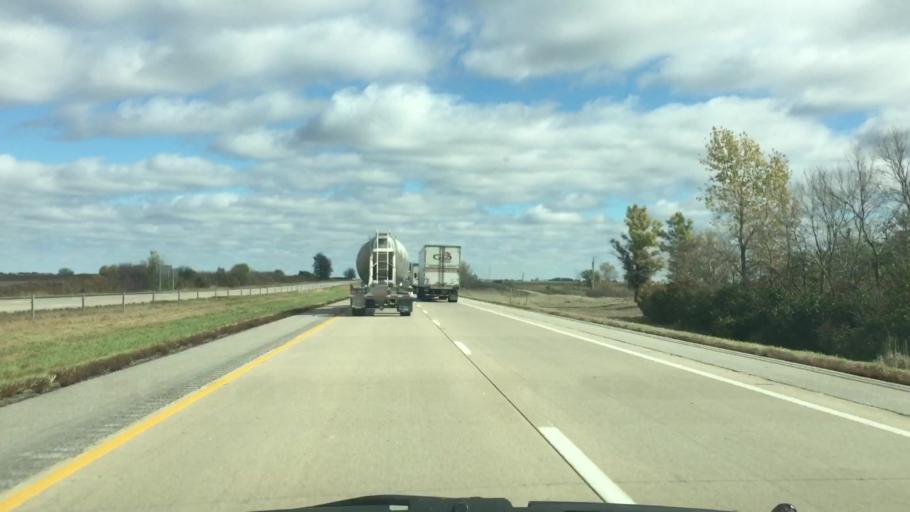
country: US
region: Iowa
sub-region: Poweshiek County
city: Brooklyn
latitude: 41.6960
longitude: -92.4229
